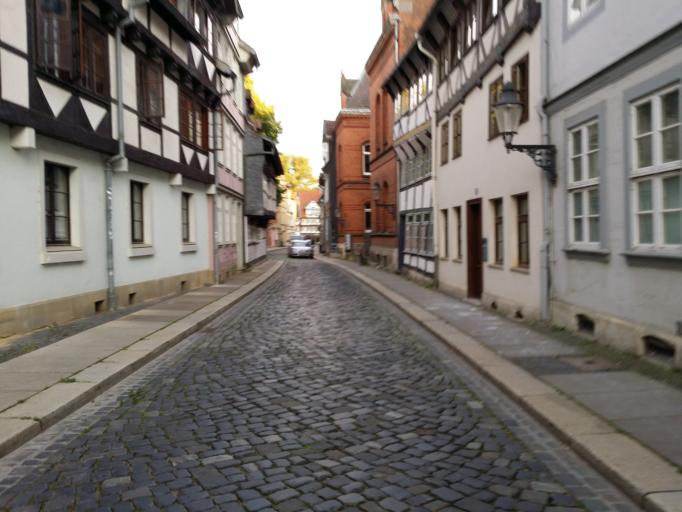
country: DE
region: Lower Saxony
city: Braunschweig
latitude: 52.2610
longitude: 10.5142
